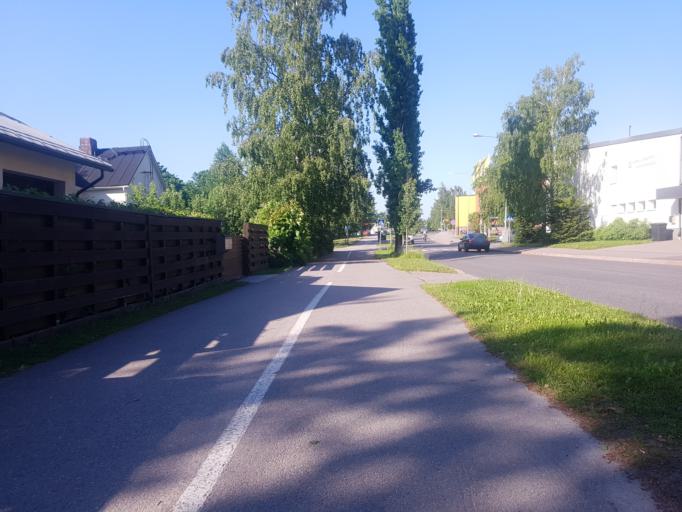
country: FI
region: Uusimaa
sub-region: Helsinki
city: Vantaa
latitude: 60.2557
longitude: 24.9965
